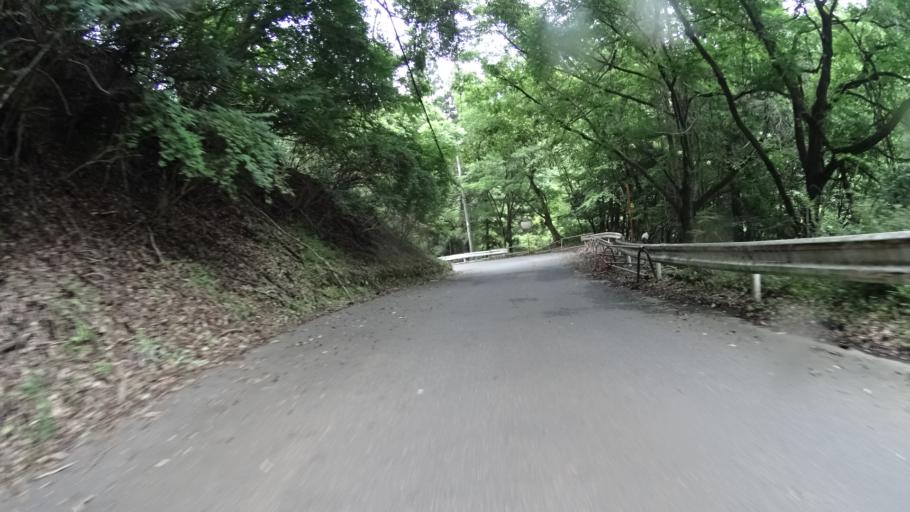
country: JP
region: Kanagawa
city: Hadano
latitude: 35.4859
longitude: 139.2190
